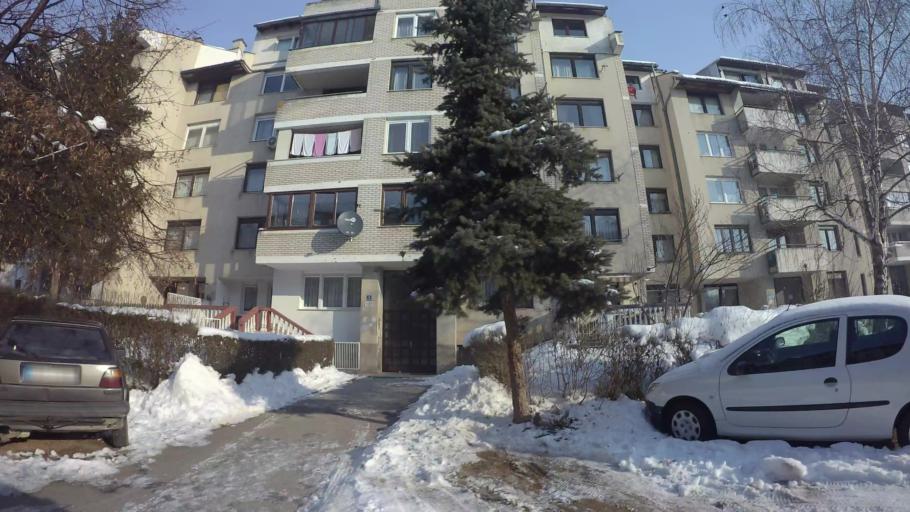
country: BA
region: Federation of Bosnia and Herzegovina
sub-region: Kanton Sarajevo
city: Sarajevo
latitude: 43.8276
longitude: 18.3577
